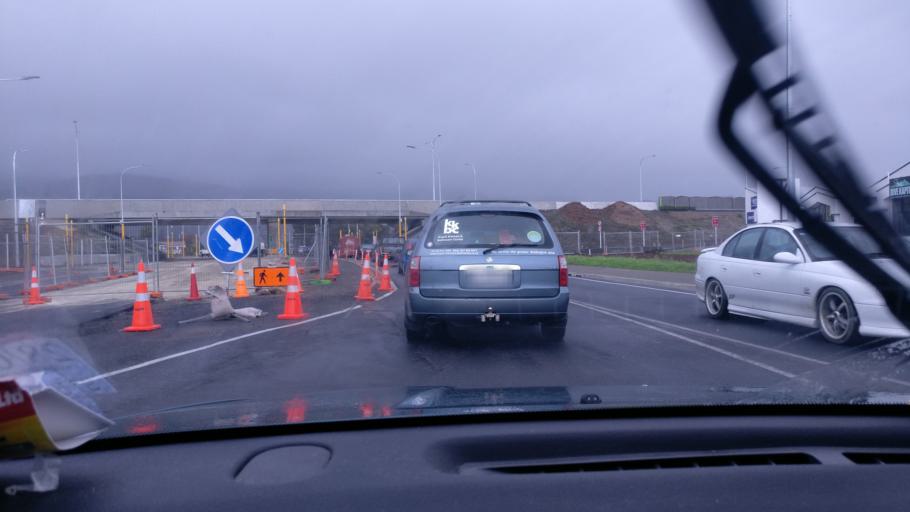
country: NZ
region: Wellington
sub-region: Kapiti Coast District
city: Paraparaumu
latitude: -40.9077
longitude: 174.9990
